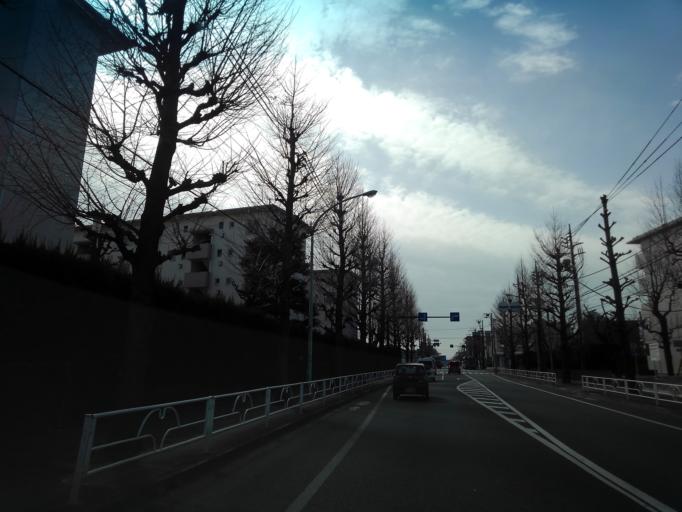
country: JP
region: Tokyo
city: Tanashicho
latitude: 35.7469
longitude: 139.5042
